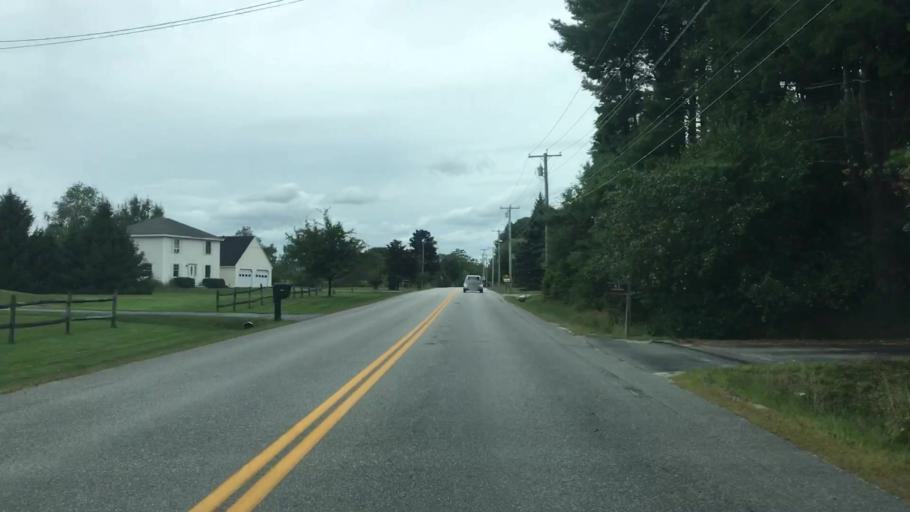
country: US
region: Maine
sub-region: Cumberland County
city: Yarmouth
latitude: 43.8389
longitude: -70.2067
